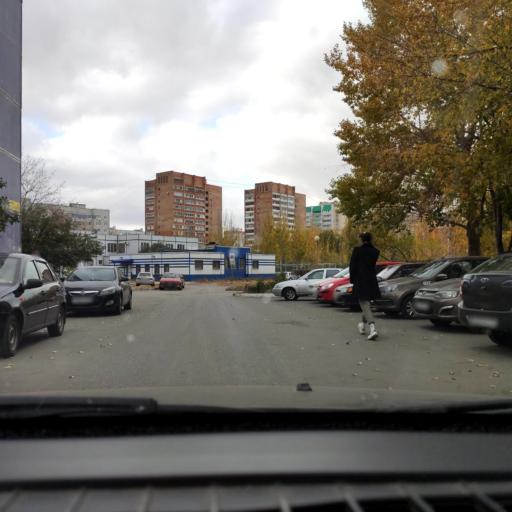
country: RU
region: Samara
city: Tol'yatti
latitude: 53.5431
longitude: 49.3346
